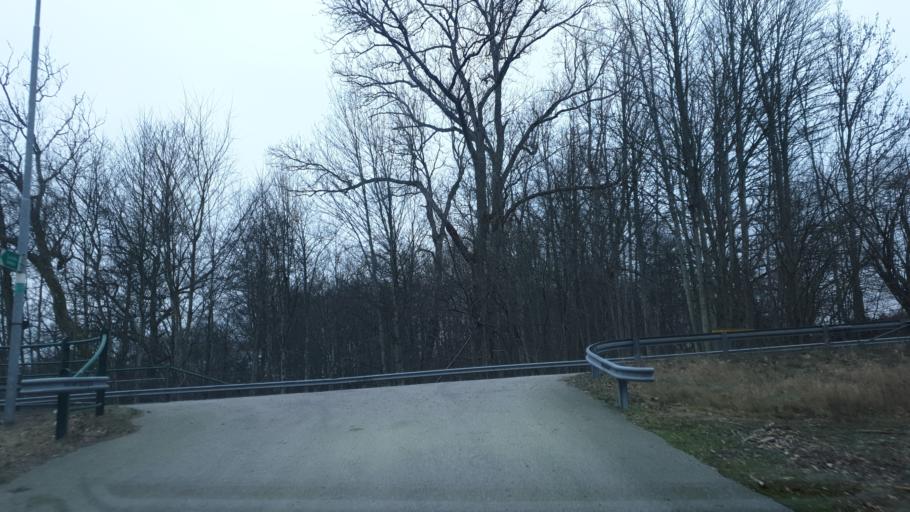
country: SE
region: Blekinge
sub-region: Karlskrona Kommun
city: Rodeby
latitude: 56.2171
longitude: 15.6731
